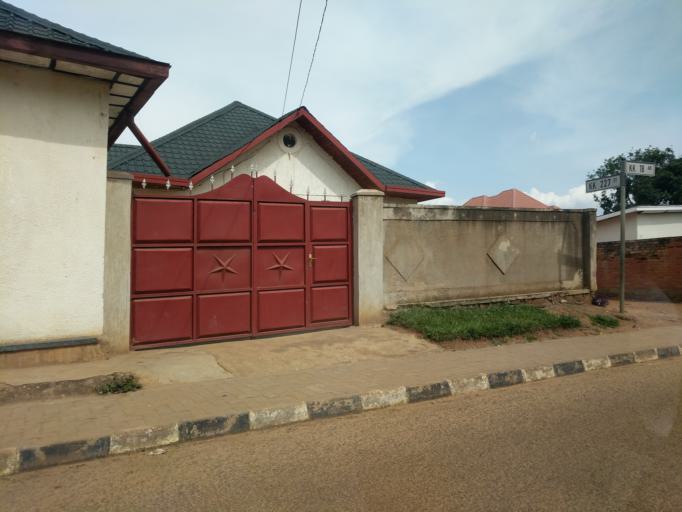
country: RW
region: Kigali
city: Kigali
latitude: -1.9855
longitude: 30.1319
